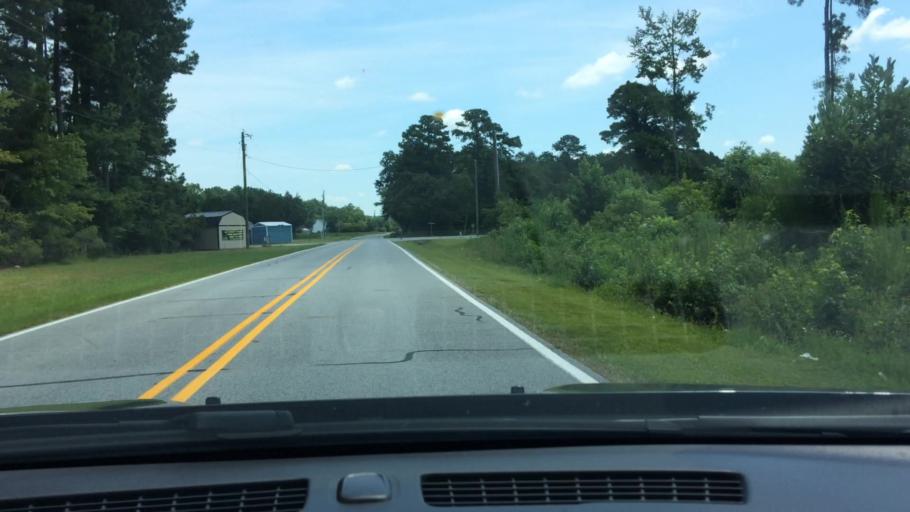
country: US
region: North Carolina
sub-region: Pitt County
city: Windsor
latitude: 35.4969
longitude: -77.3437
